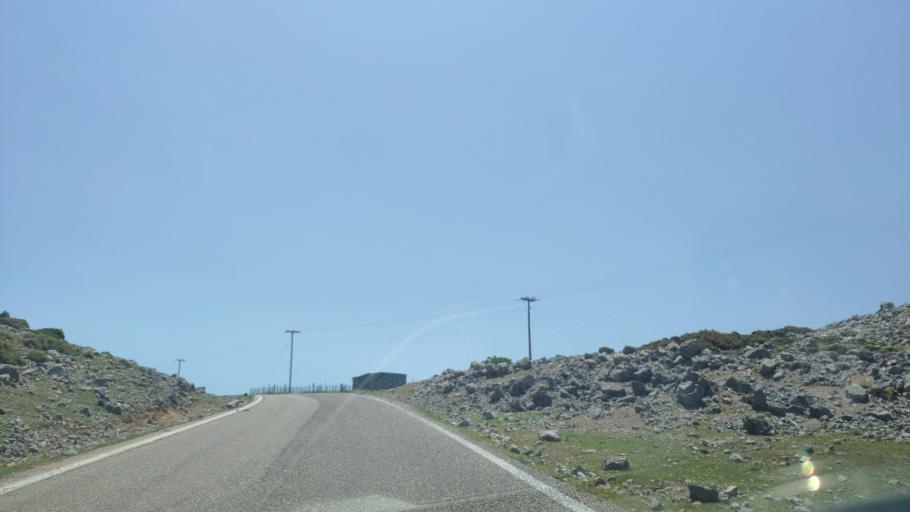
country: GR
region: West Greece
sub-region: Nomos Aitolias kai Akarnanias
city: Krikellos
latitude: 39.0507
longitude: 21.3724
